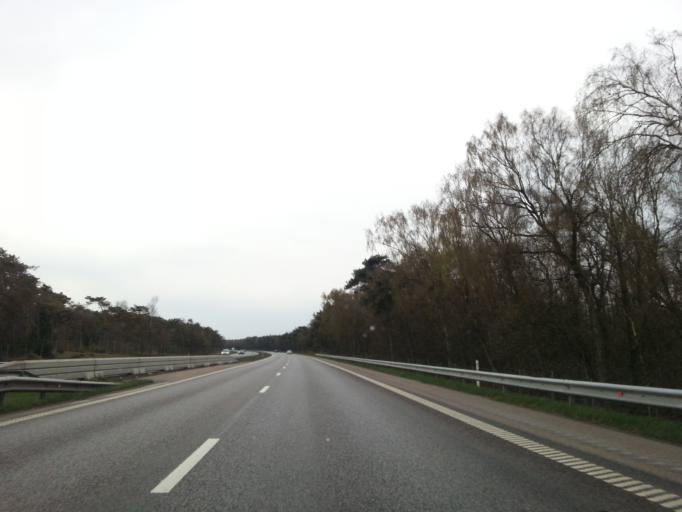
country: SE
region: Halland
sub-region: Halmstads Kommun
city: Paarp
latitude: 56.5754
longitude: 12.9485
